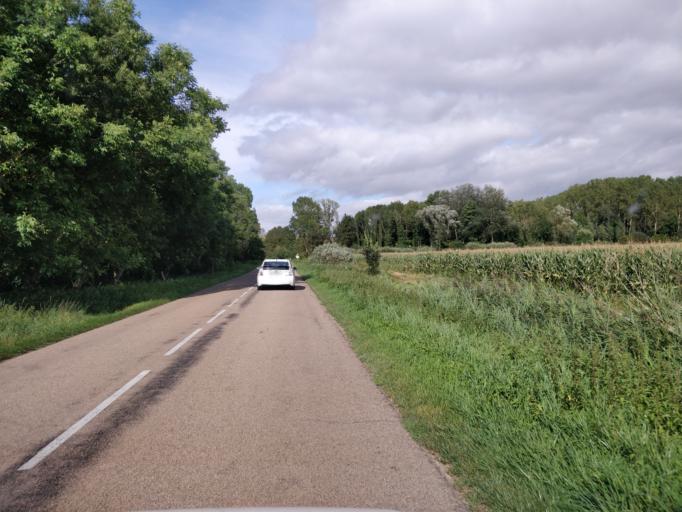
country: FR
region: Champagne-Ardenne
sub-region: Departement de l'Aube
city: Aix-en-Othe
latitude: 48.2288
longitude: 3.6203
